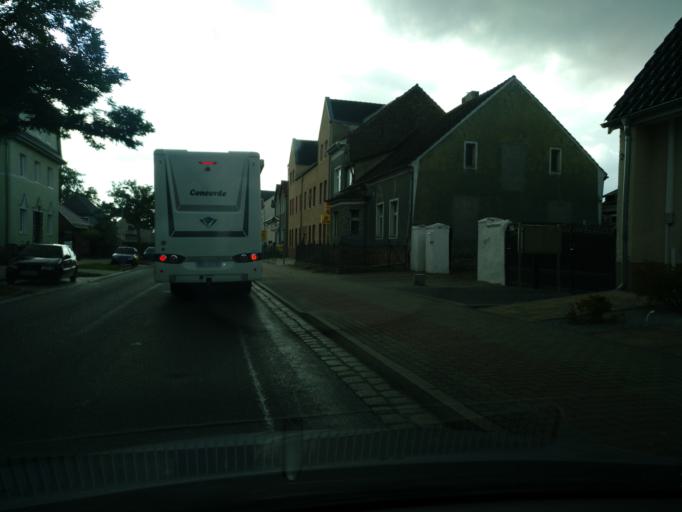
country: DE
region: Brandenburg
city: Woltersdorf
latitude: 52.4808
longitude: 13.7744
